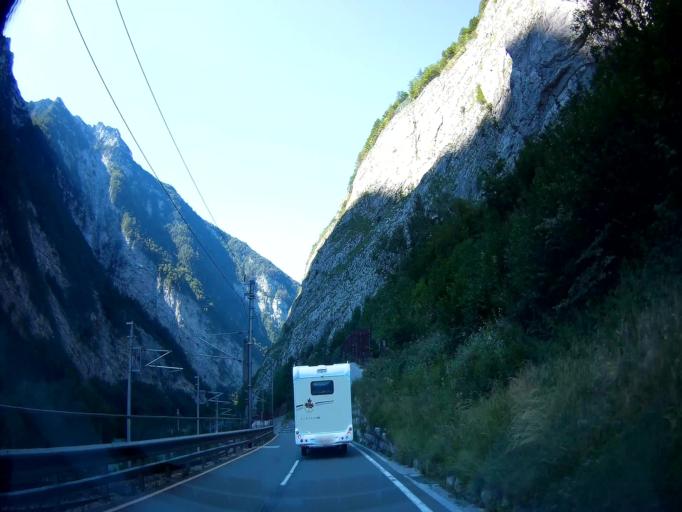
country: AT
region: Salzburg
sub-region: Politischer Bezirk Hallein
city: Golling an der Salzach
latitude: 47.5515
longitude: 13.1702
